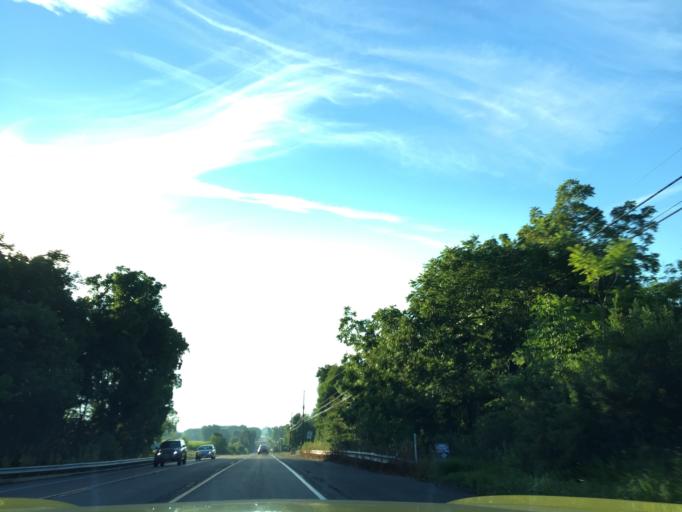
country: US
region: Pennsylvania
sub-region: Lehigh County
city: Breinigsville
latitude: 40.5421
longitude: -75.6514
